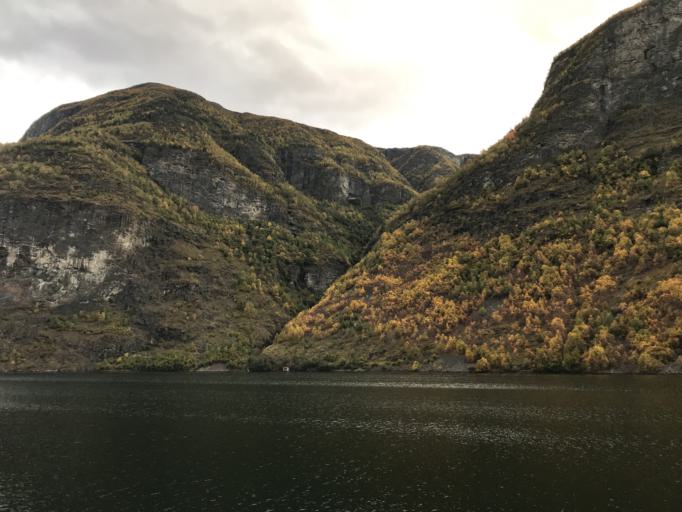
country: NO
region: Sogn og Fjordane
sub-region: Aurland
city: Aurlandsvangen
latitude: 60.9624
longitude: 7.1010
